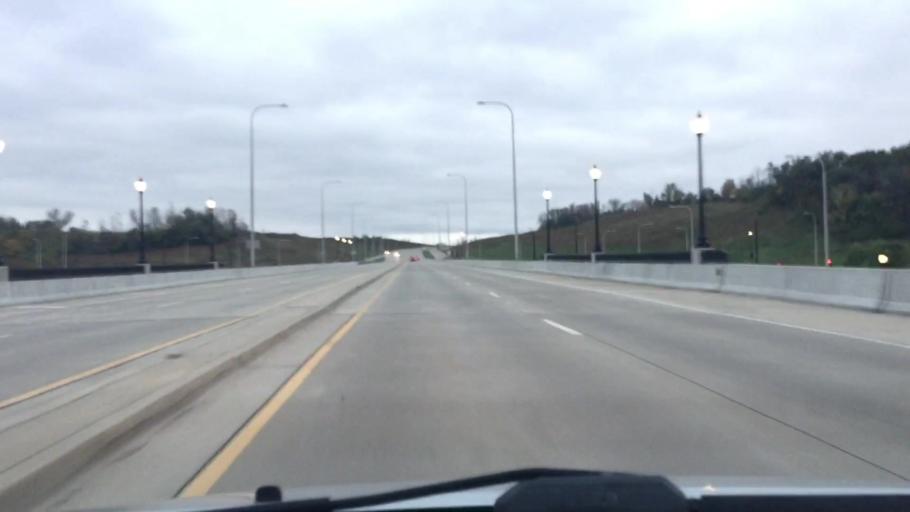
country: US
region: Illinois
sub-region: McHenry County
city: Algonquin
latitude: 42.1681
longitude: -88.2970
